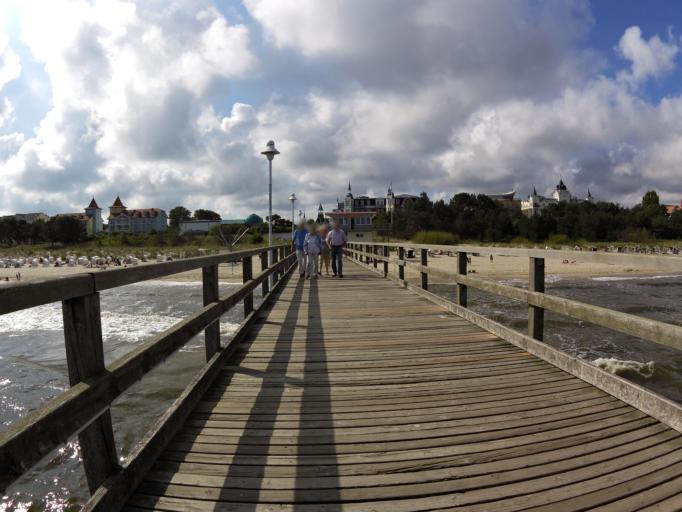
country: DE
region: Mecklenburg-Vorpommern
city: Ostseebad Zinnowitz
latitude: 54.0826
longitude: 13.9159
